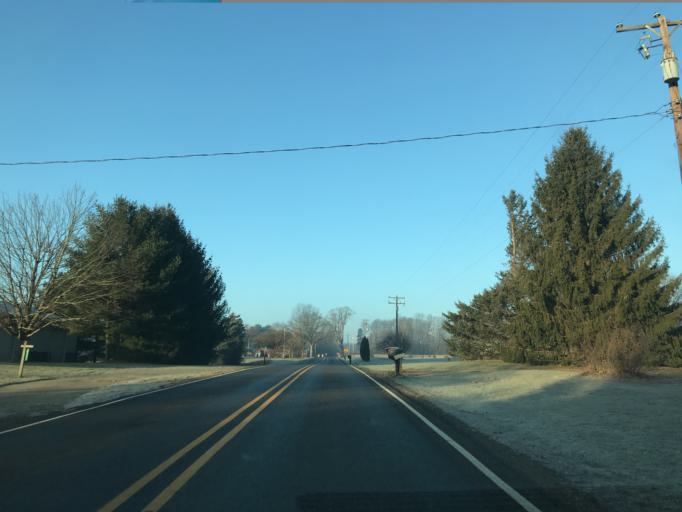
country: US
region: Michigan
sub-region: Ingham County
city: Leslie
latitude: 42.3787
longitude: -84.4434
